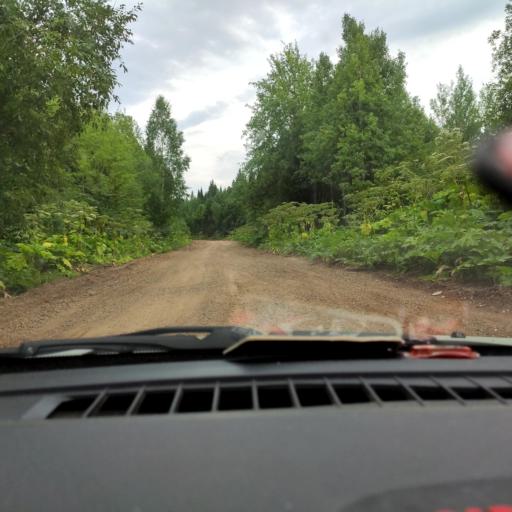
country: RU
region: Perm
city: Kultayevo
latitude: 57.8156
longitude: 56.0009
